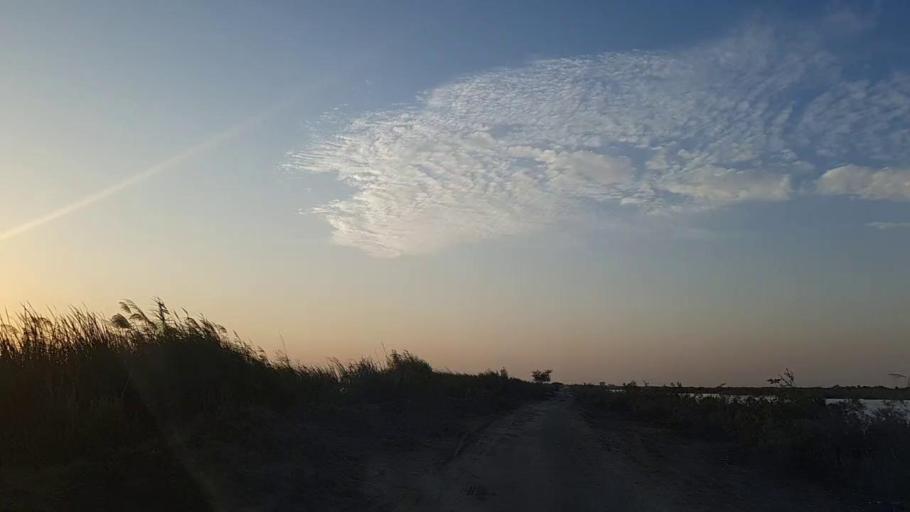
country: PK
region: Sindh
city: Chuhar Jamali
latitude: 24.4630
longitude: 68.1046
